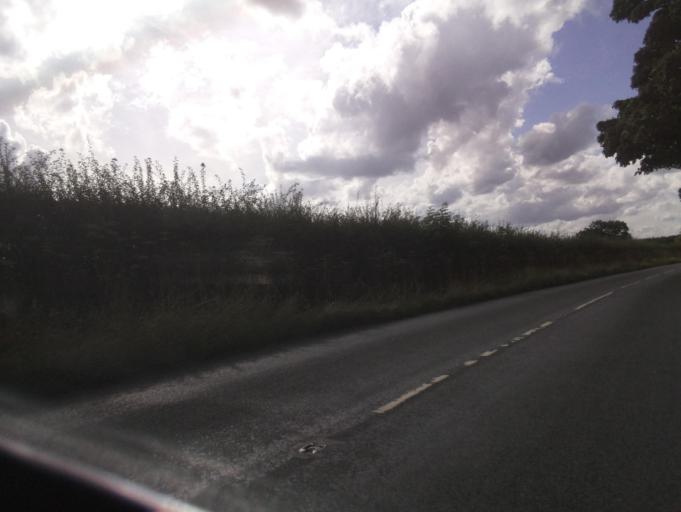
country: GB
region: England
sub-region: North Yorkshire
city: Bedale
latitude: 54.2092
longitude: -1.6125
